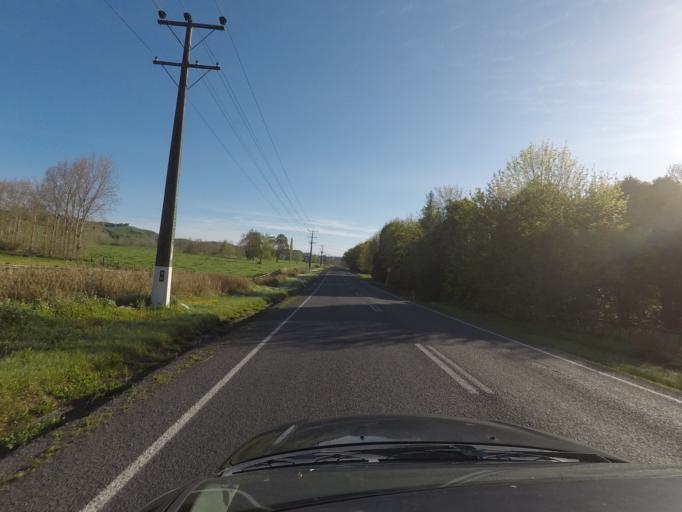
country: NZ
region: Auckland
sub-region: Auckland
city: Red Hill
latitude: -37.0107
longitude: 174.9516
